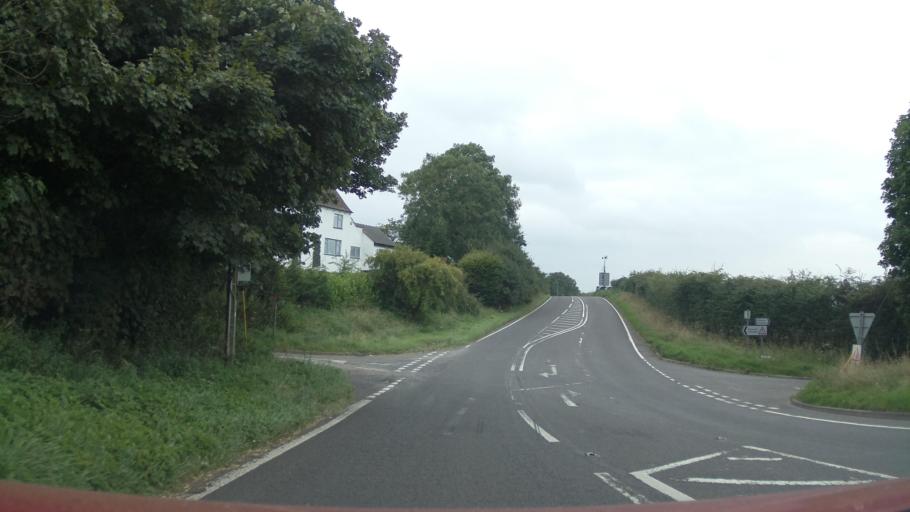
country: GB
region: England
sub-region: Derbyshire
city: Bradley
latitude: 53.0148
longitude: -1.6792
